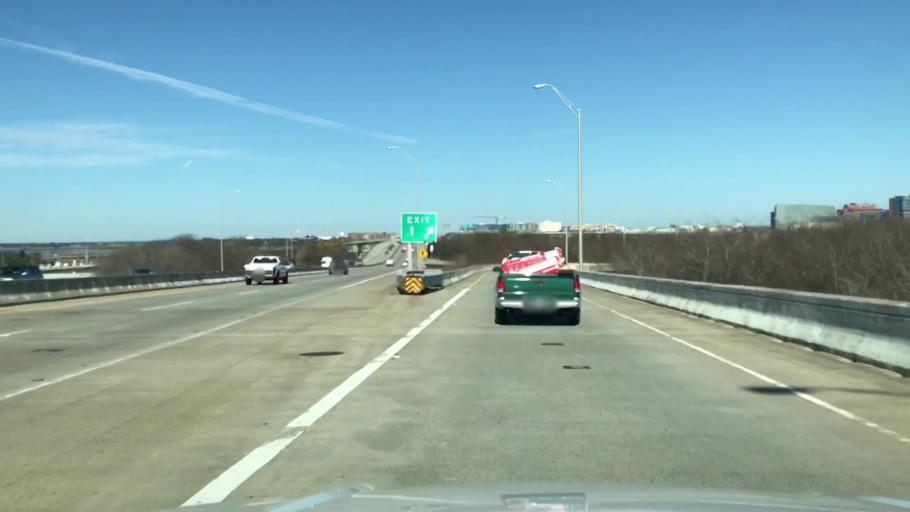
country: US
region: South Carolina
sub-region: Charleston County
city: Charleston
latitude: 32.7722
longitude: -79.9580
